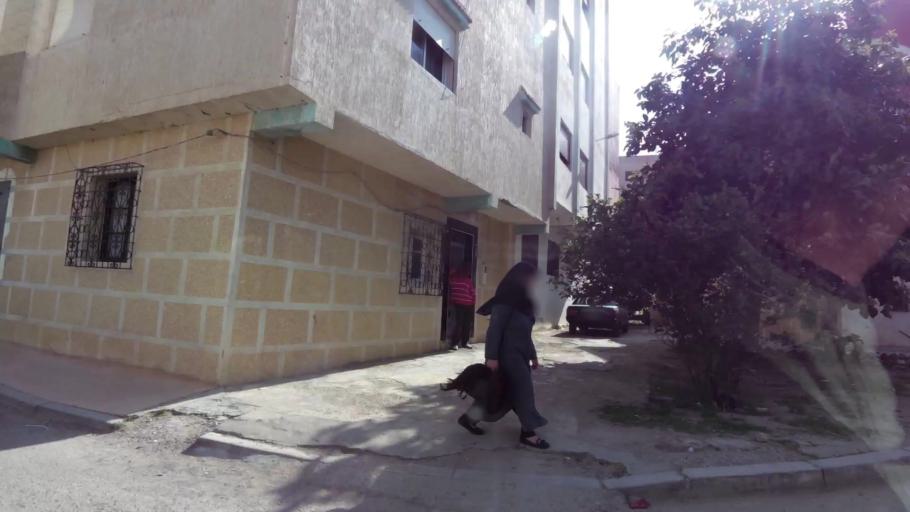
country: MA
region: Tanger-Tetouan
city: Tetouan
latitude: 35.5892
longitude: -5.3473
